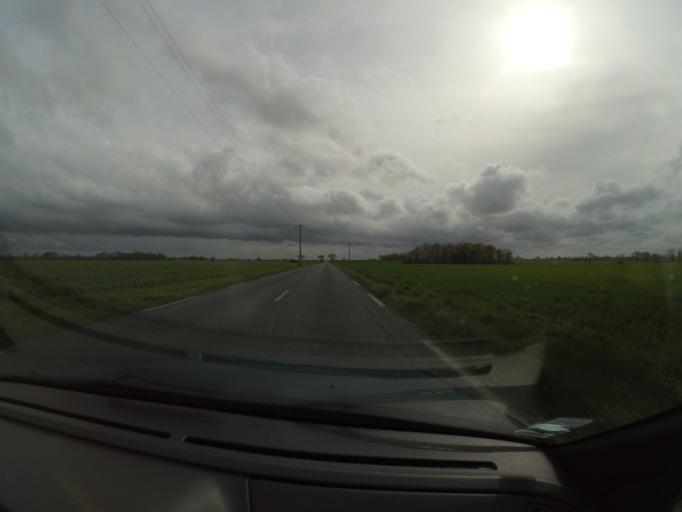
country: FR
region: Pays de la Loire
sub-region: Departement de Maine-et-Loire
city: Saint-Laurent-des-Autels
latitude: 47.2580
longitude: -1.2039
